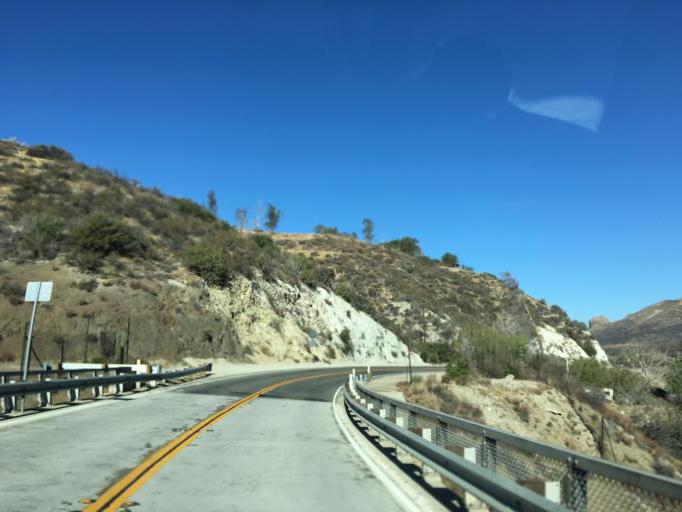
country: US
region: California
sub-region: Los Angeles County
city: Acton
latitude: 34.4383
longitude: -118.2490
